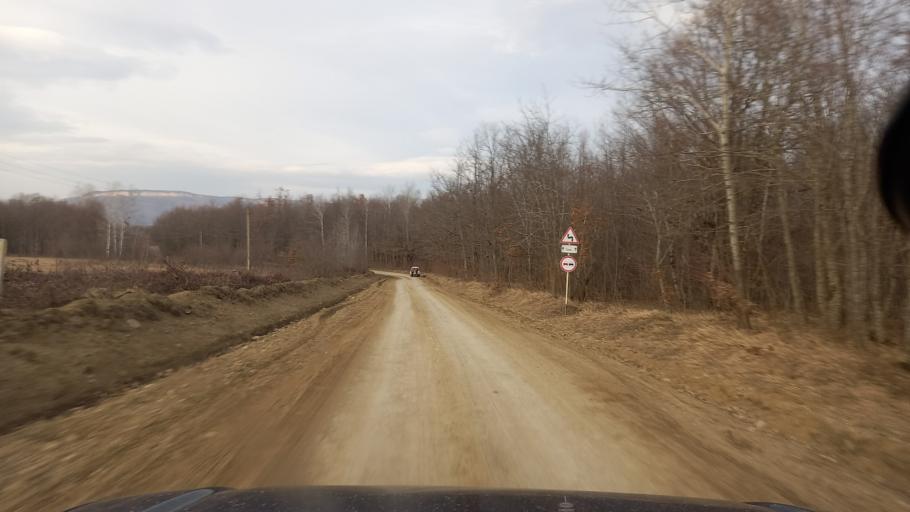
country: RU
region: Adygeya
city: Kamennomostskiy
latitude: 44.1601
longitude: 40.2448
